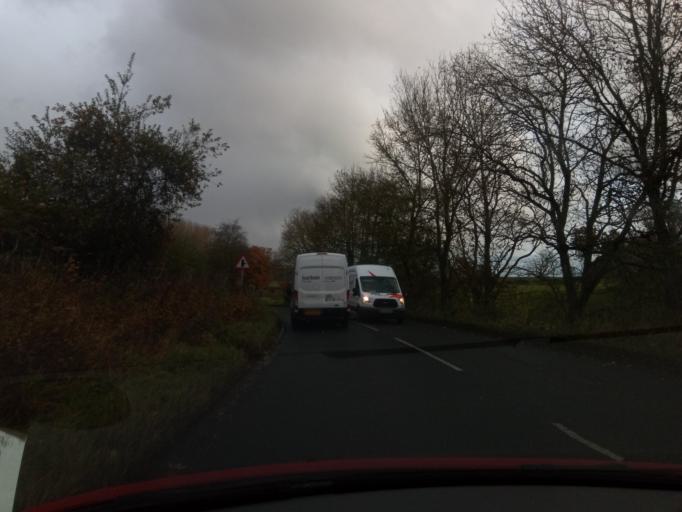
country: GB
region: England
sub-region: Northumberland
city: Birtley
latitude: 55.0548
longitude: -2.1868
